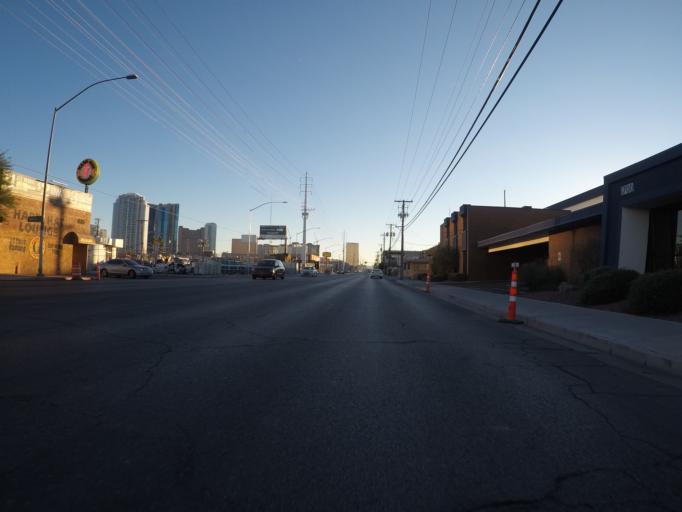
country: US
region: Nevada
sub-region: Clark County
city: Las Vegas
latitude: 36.1513
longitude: -115.1601
